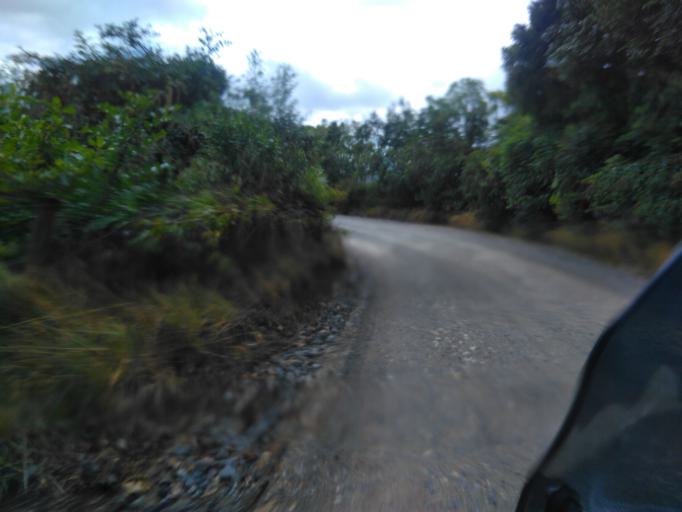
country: NZ
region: Gisborne
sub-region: Gisborne District
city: Gisborne
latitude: -38.2407
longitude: 178.0700
